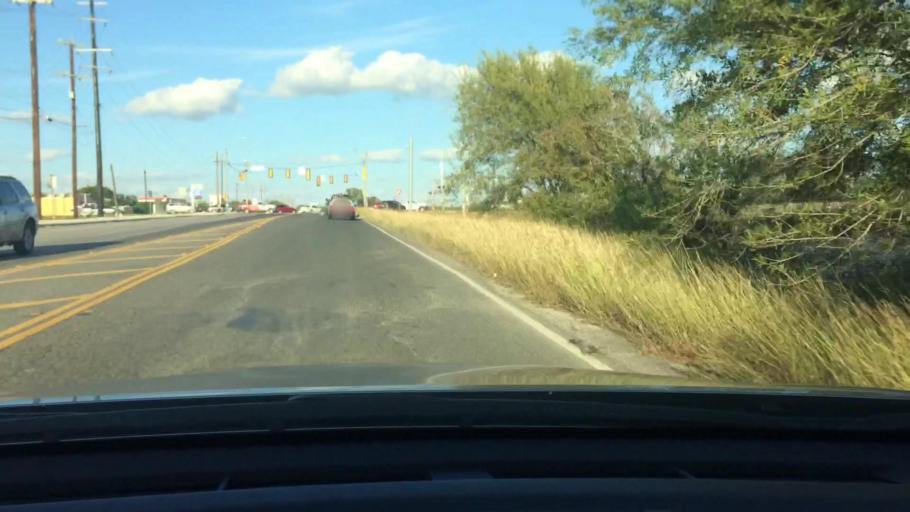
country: US
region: Texas
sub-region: Bexar County
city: Windcrest
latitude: 29.4965
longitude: -98.3504
